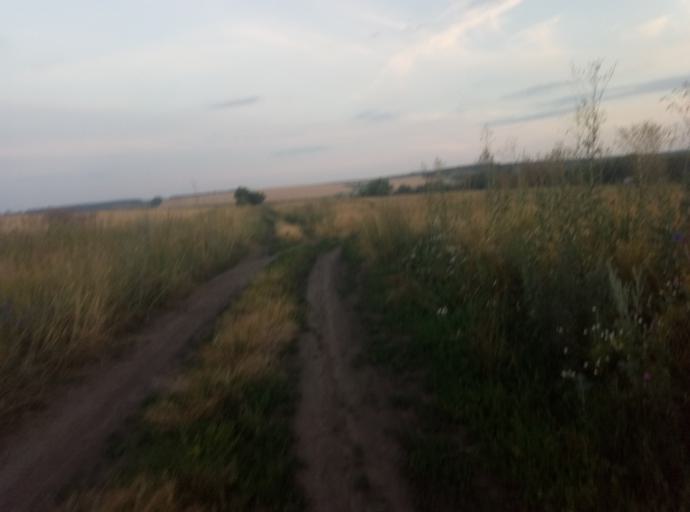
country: RU
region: Tula
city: Kireyevsk
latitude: 53.7976
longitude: 37.8685
